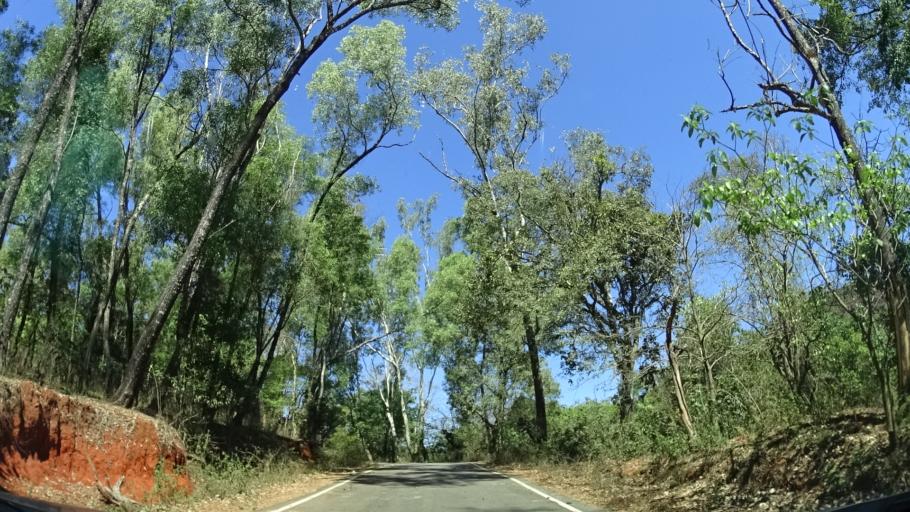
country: IN
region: Karnataka
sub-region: Chikmagalur
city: Sringeri
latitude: 13.2116
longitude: 75.2720
